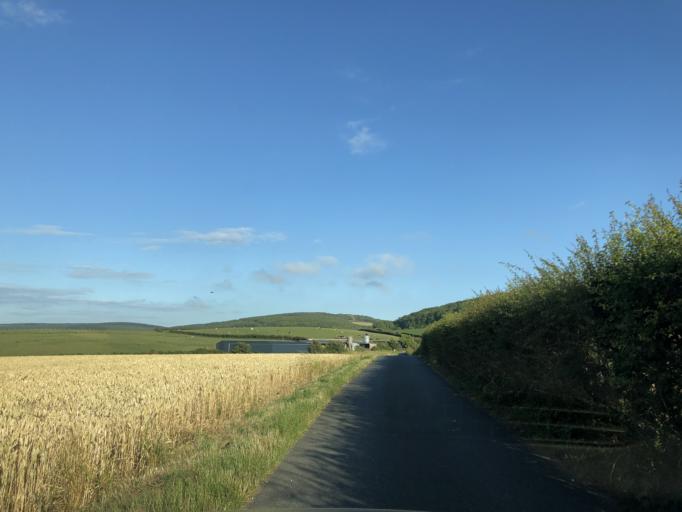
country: GB
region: England
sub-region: Isle of Wight
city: Shalfleet
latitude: 50.6743
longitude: -1.4529
